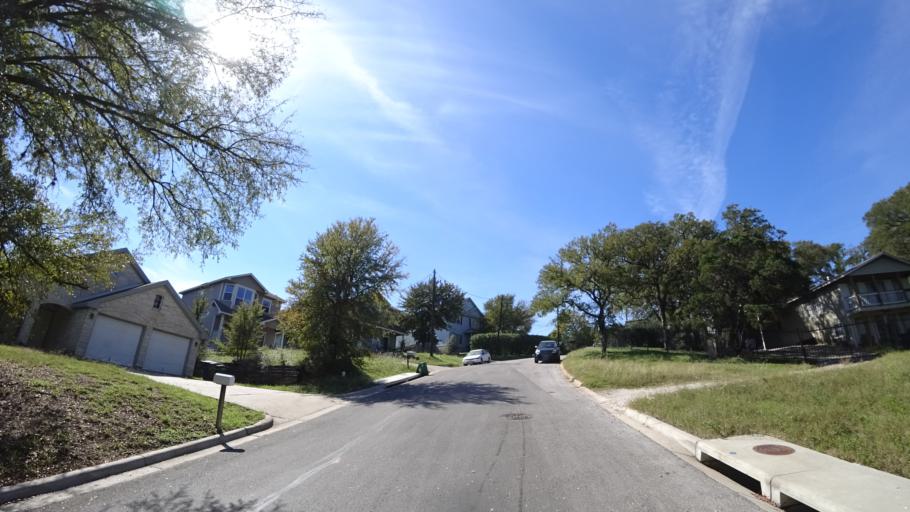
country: US
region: Texas
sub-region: Travis County
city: Austin
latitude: 30.2733
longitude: -97.6814
